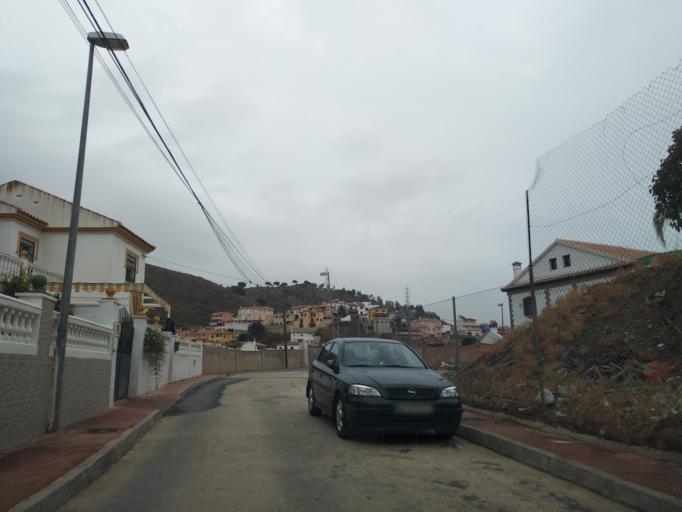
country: ES
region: Andalusia
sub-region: Provincia de Malaga
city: Malaga
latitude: 36.7480
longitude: -4.4777
